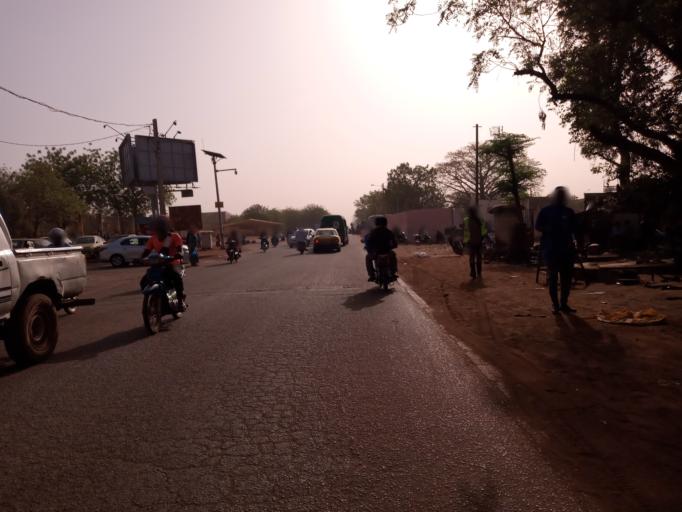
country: ML
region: Bamako
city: Bamako
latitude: 12.6582
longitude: -7.9938
